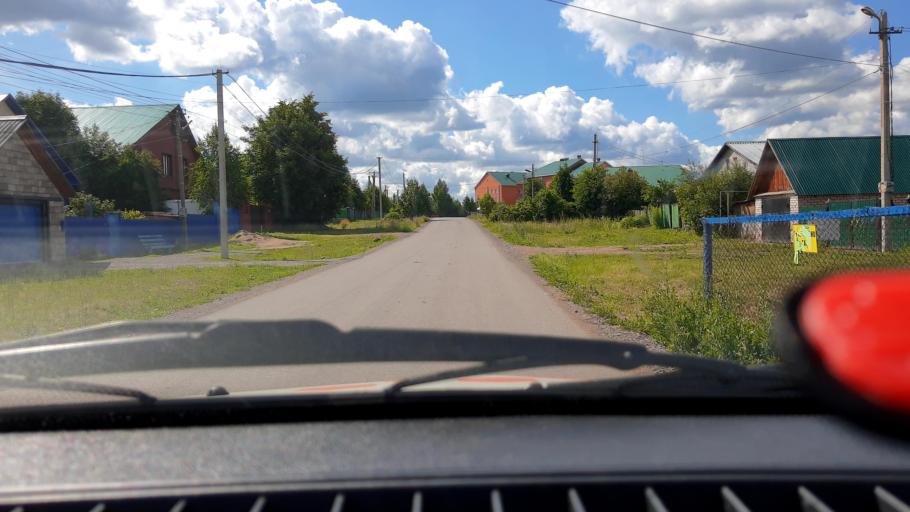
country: RU
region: Bashkortostan
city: Avdon
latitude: 54.4960
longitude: 55.8961
